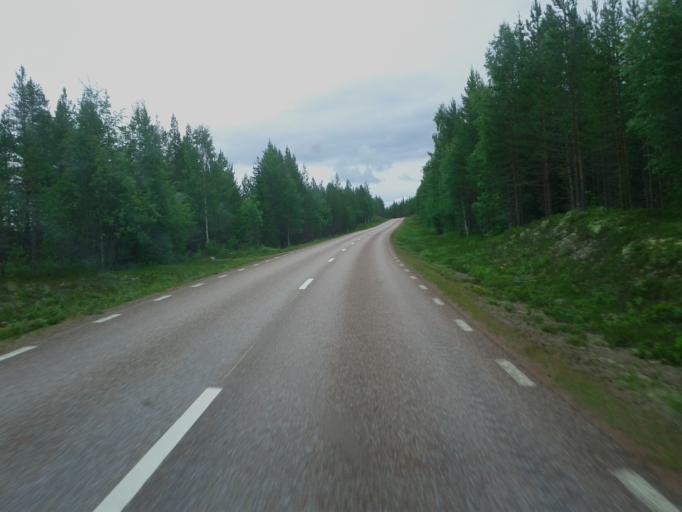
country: NO
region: Hedmark
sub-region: Trysil
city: Innbygda
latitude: 61.7149
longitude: 13.0065
